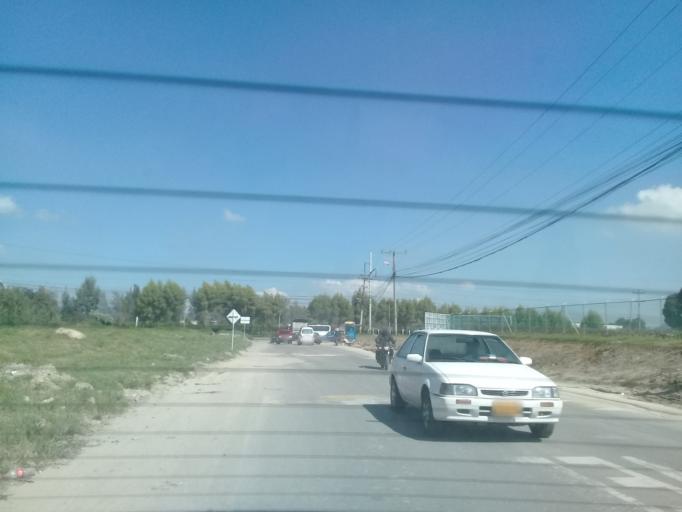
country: CO
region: Cundinamarca
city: Funza
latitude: 4.7484
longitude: -74.1637
